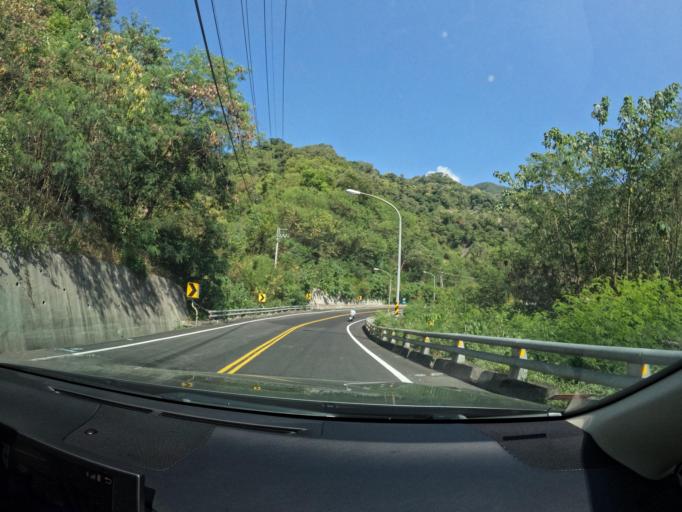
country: TW
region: Taiwan
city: Yujing
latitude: 23.1405
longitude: 120.7405
